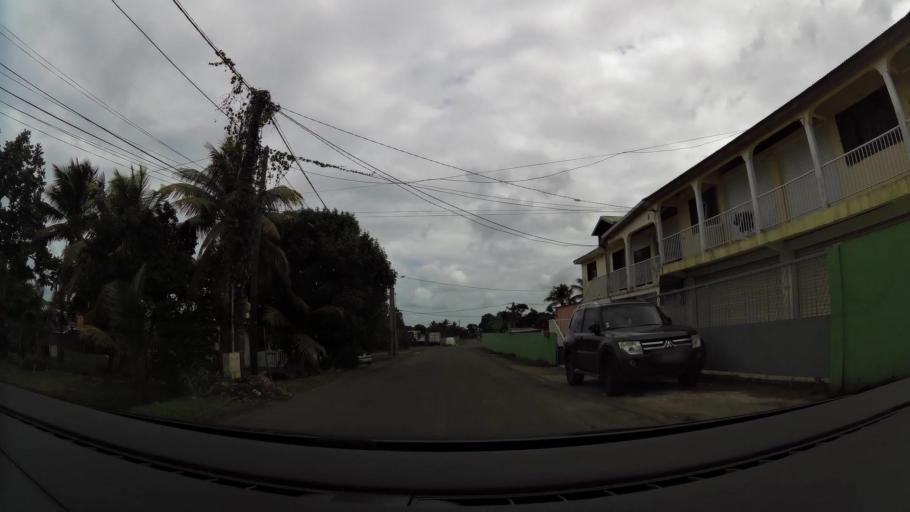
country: GP
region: Guadeloupe
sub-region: Guadeloupe
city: Sainte-Rose
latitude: 16.3233
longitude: -61.6964
